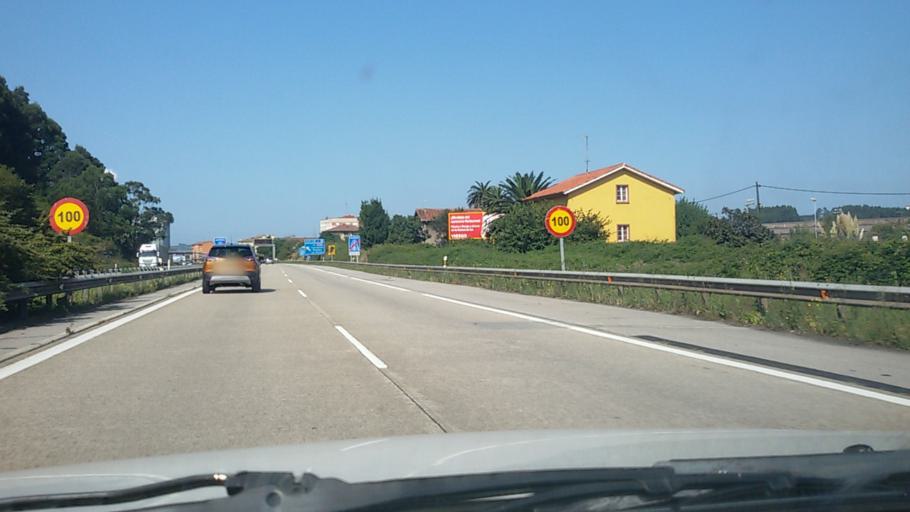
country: ES
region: Asturias
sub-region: Province of Asturias
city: Corvera de Asturias
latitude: 43.5517
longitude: -5.8815
